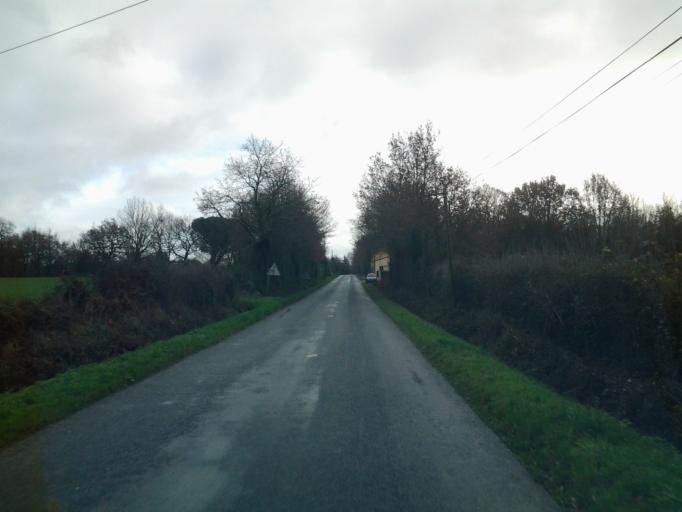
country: FR
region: Pays de la Loire
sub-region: Departement de la Vendee
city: Nesmy
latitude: 46.6467
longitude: -1.3742
